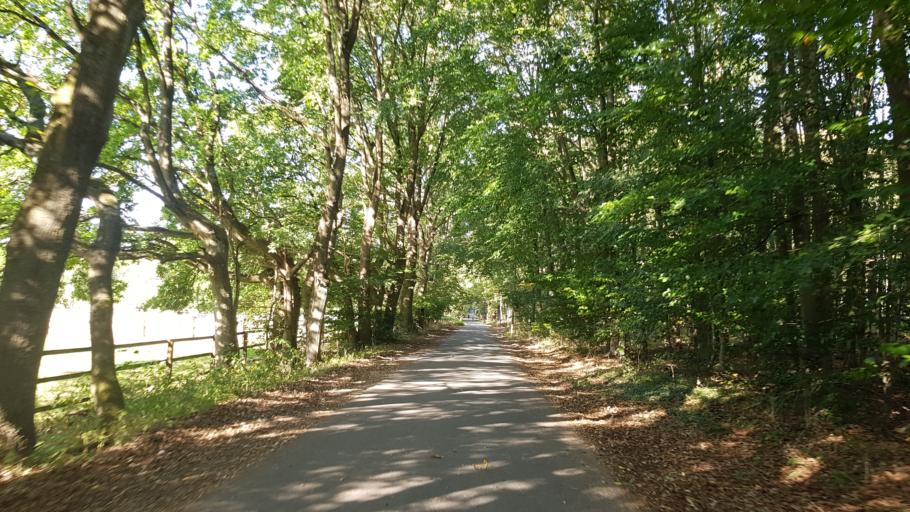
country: DE
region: North Rhine-Westphalia
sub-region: Regierungsbezirk Dusseldorf
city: Muelheim (Ruhr)
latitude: 51.3803
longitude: 6.8361
